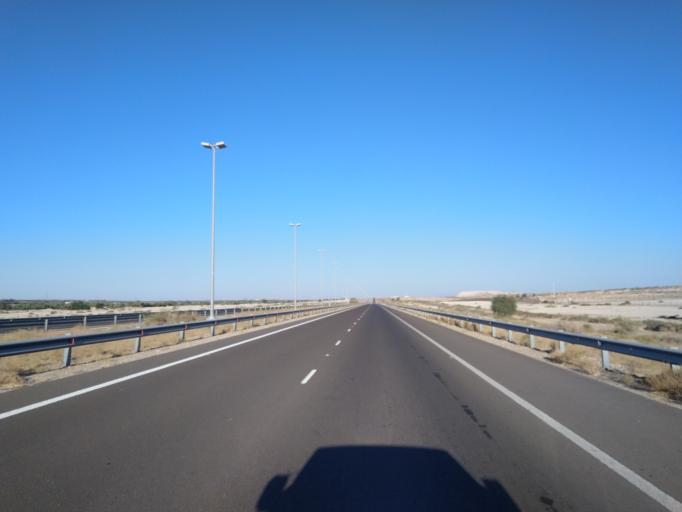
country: OM
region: Al Buraimi
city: Al Buraymi
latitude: 24.5281
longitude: 55.5614
